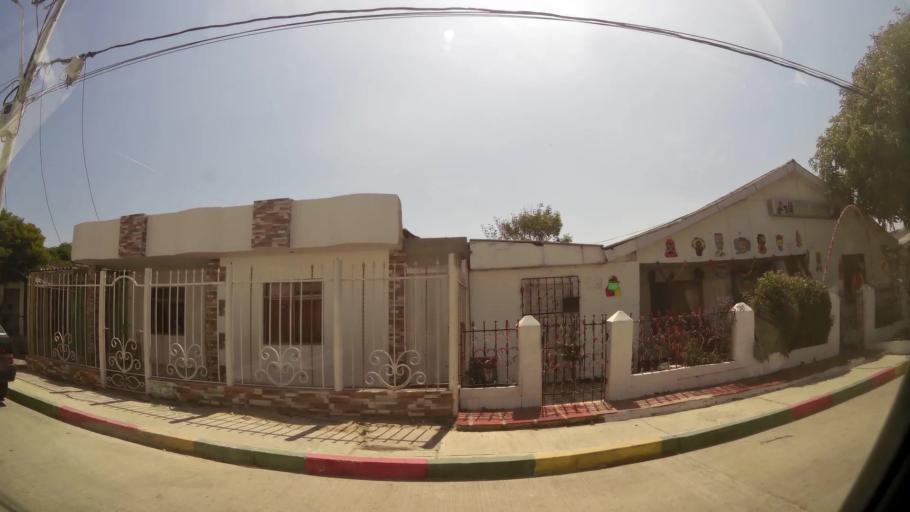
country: CO
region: Atlantico
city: Barranquilla
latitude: 10.9700
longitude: -74.8236
